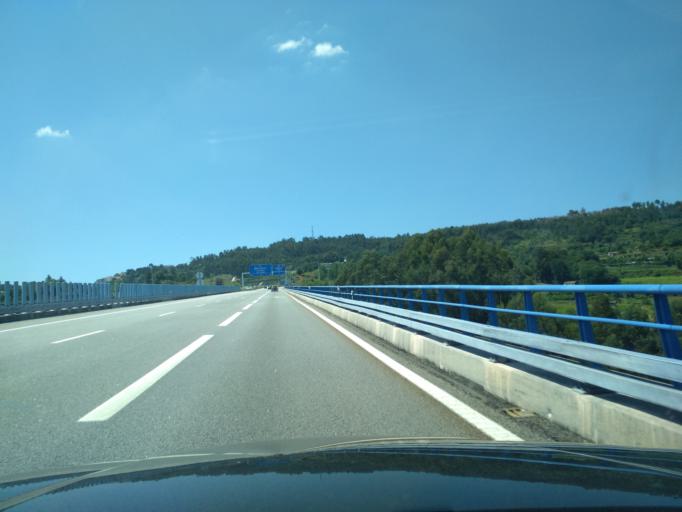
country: PT
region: Braga
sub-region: Vizela
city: Vizela
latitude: 41.4006
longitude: -8.2488
